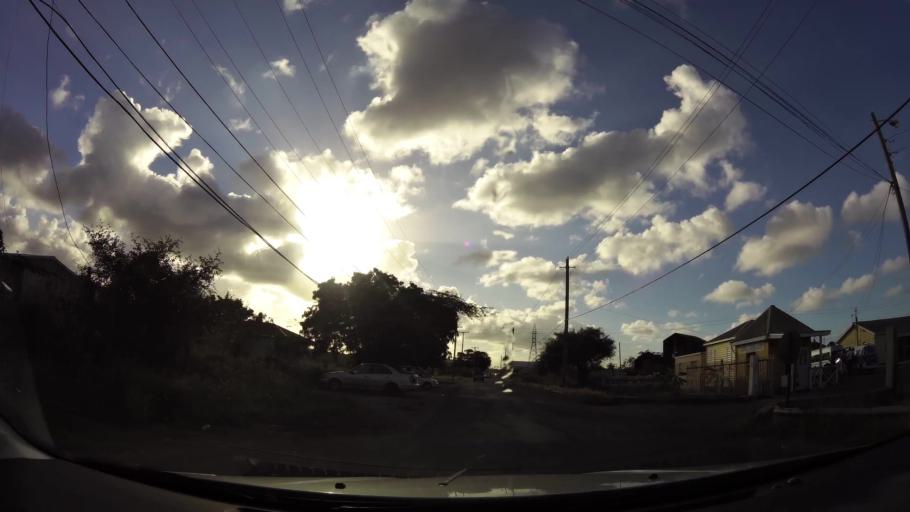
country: AG
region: Saint George
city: Piggotts
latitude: 17.1265
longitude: -61.8107
